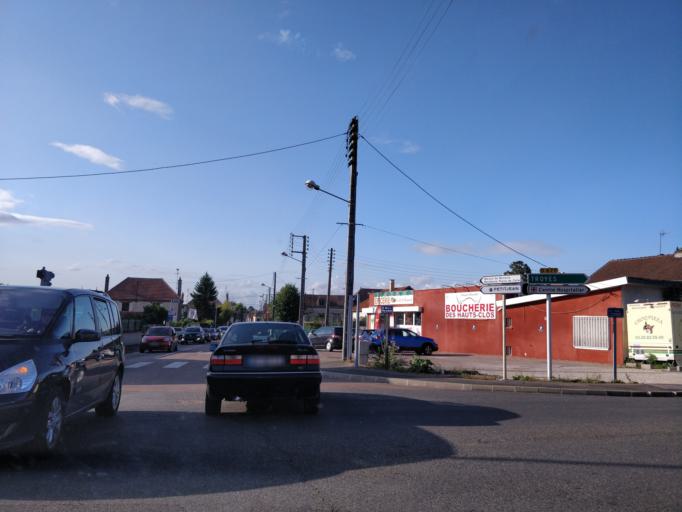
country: FR
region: Champagne-Ardenne
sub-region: Departement de l'Aube
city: Saint-Andre-les-Vergers
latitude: 48.2742
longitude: 4.0583
